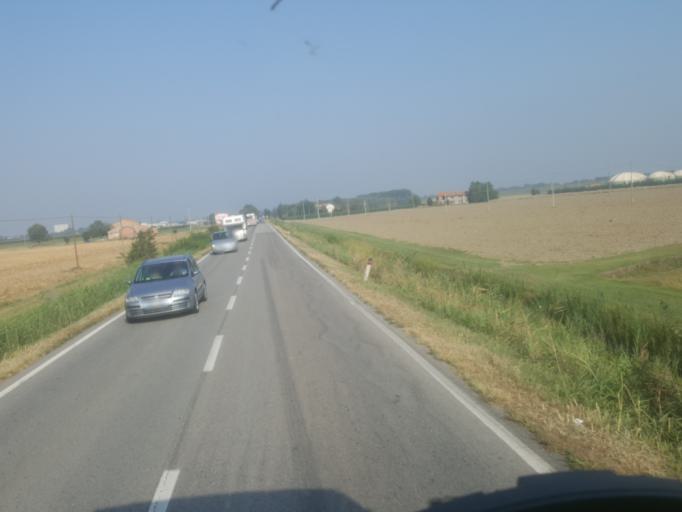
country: IT
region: Emilia-Romagna
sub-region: Provincia di Ravenna
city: Lavezzola
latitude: 44.5632
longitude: 11.9044
